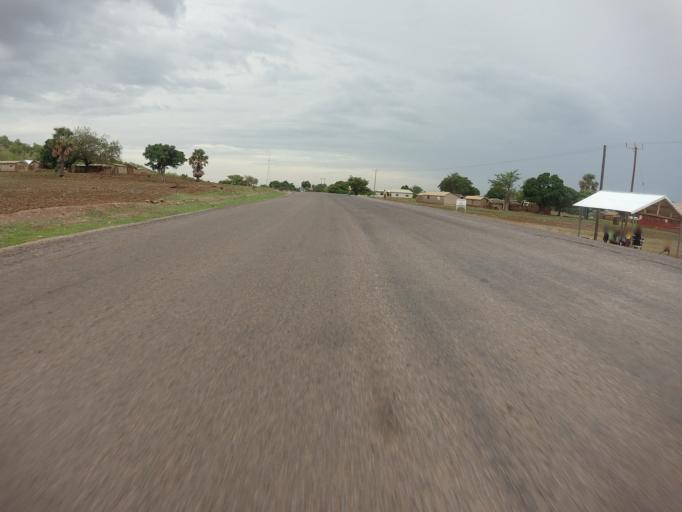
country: GH
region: Upper East
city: Bolgatanga
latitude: 10.8440
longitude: -0.6857
